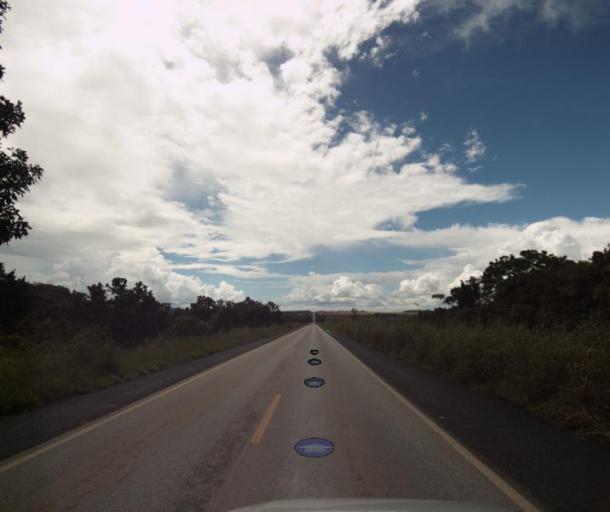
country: BR
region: Goias
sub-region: Uruacu
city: Uruacu
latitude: -14.2054
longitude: -49.1299
